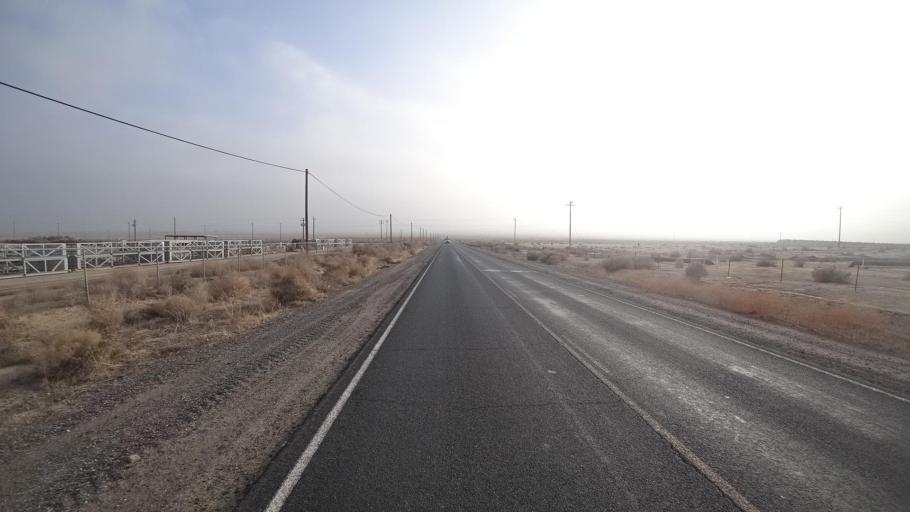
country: US
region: California
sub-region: Kern County
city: Ford City
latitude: 35.2322
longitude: -119.4456
